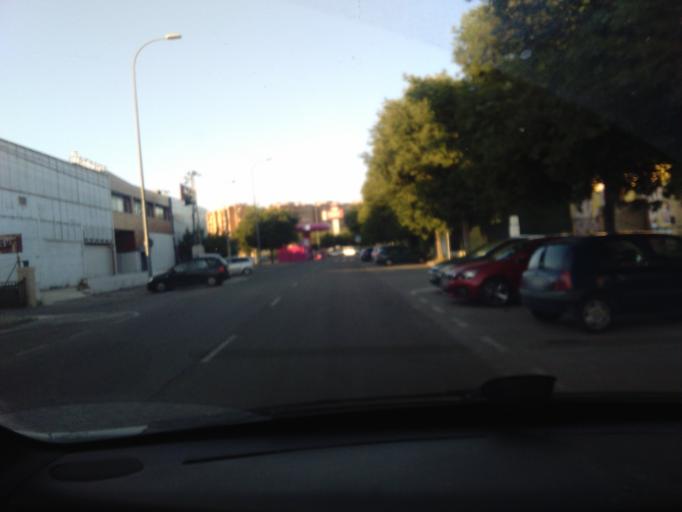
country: ES
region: Andalusia
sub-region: Provincia de Sevilla
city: Sevilla
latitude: 37.3954
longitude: -5.9465
